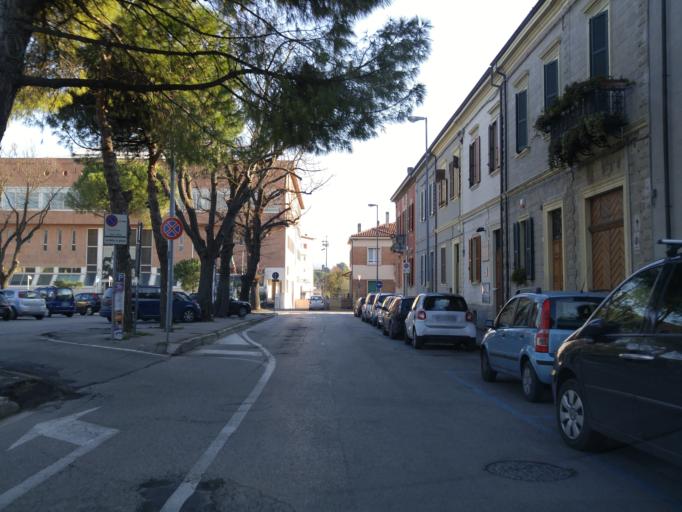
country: IT
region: The Marches
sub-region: Provincia di Pesaro e Urbino
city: Pesaro
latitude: 43.9060
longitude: 12.9121
